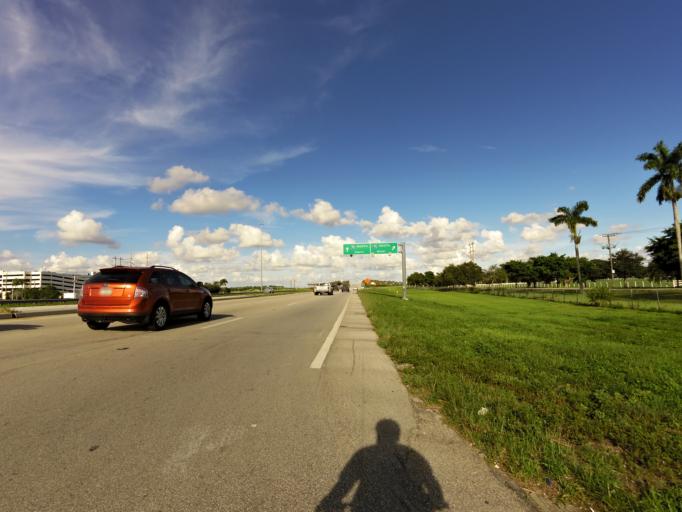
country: US
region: Florida
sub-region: Broward County
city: Southwest Ranches
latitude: 26.0624
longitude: -80.3612
